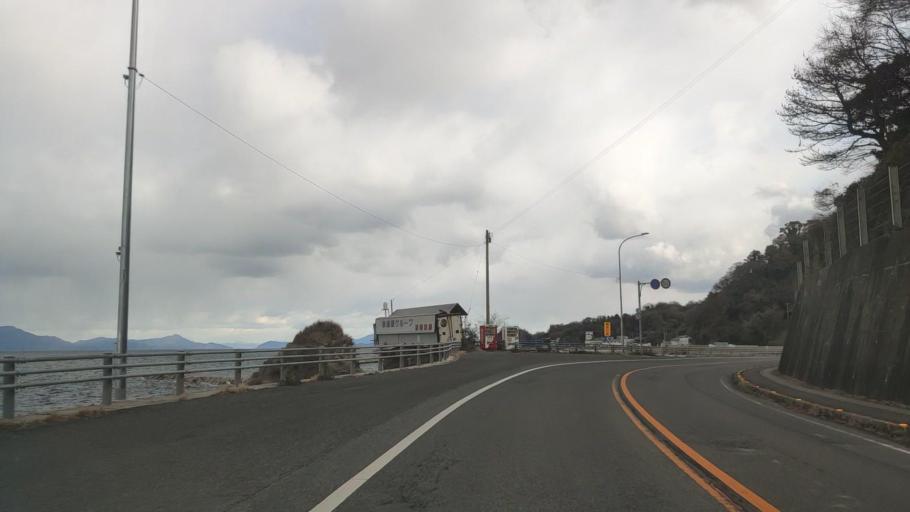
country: JP
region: Ehime
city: Hojo
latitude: 34.0263
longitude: 132.8223
